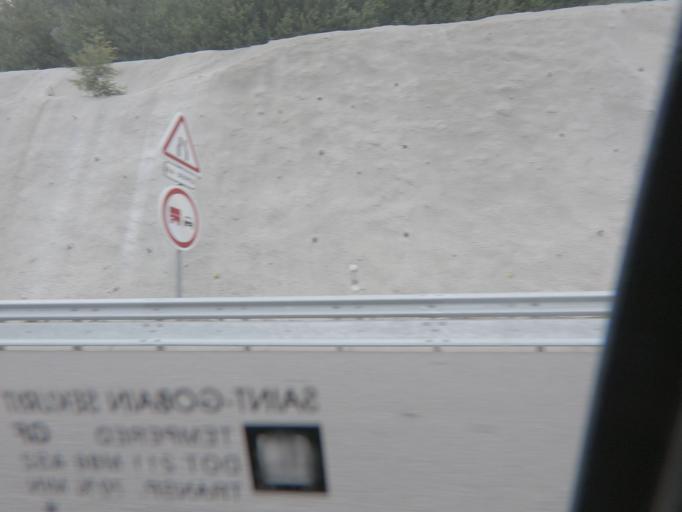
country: PT
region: Vila Real
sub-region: Santa Marta de Penaguiao
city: Santa Marta de Penaguiao
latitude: 41.2791
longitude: -7.8647
